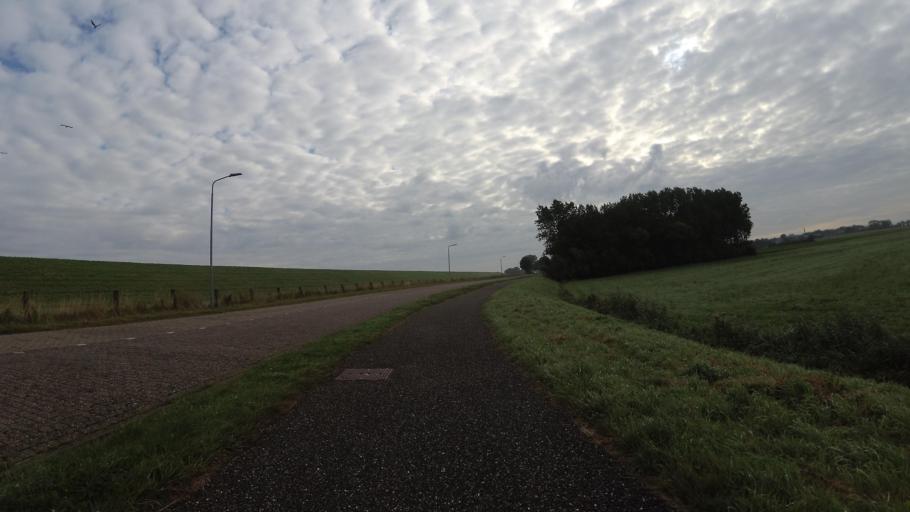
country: NL
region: North Holland
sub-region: Gemeente Hollands Kroon
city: Den Oever
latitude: 52.9333
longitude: 5.0150
